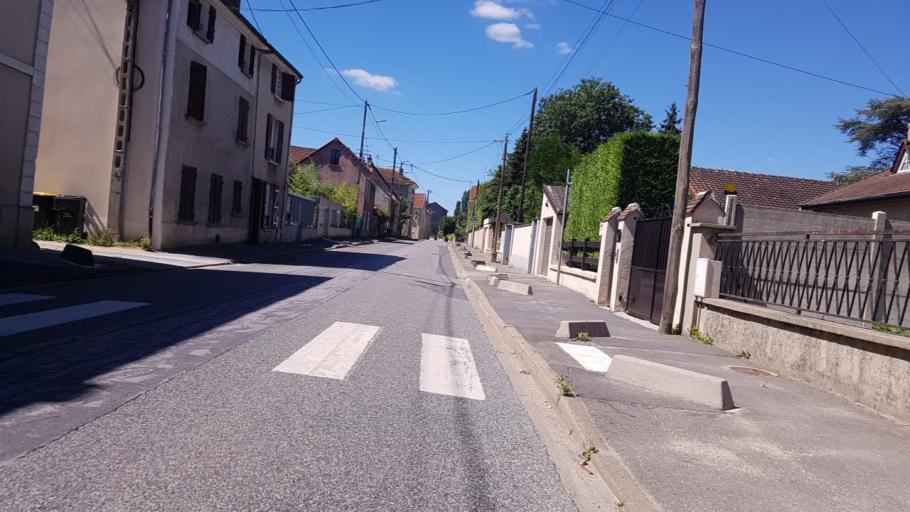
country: FR
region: Ile-de-France
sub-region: Departement de Seine-et-Marne
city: Chamigny
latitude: 48.9610
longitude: 3.1462
